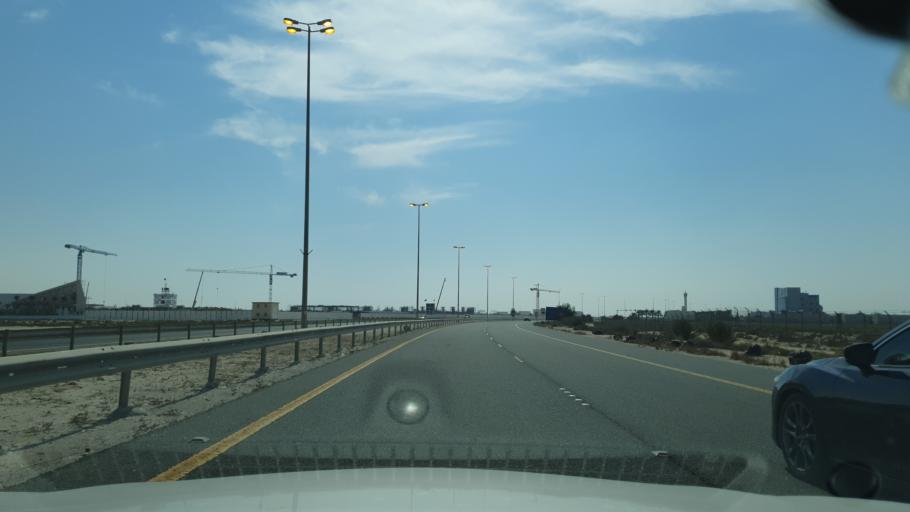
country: BH
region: Central Governorate
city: Dar Kulayb
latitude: 26.0324
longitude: 50.4992
